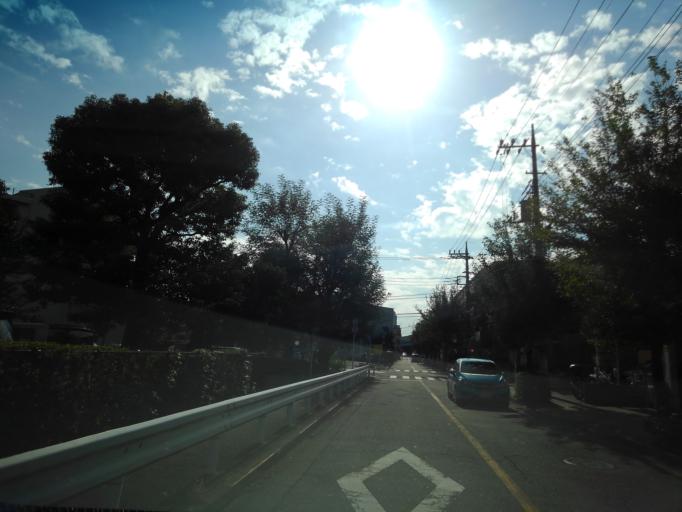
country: JP
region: Tokyo
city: Higashimurayama-shi
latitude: 35.7528
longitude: 139.4696
